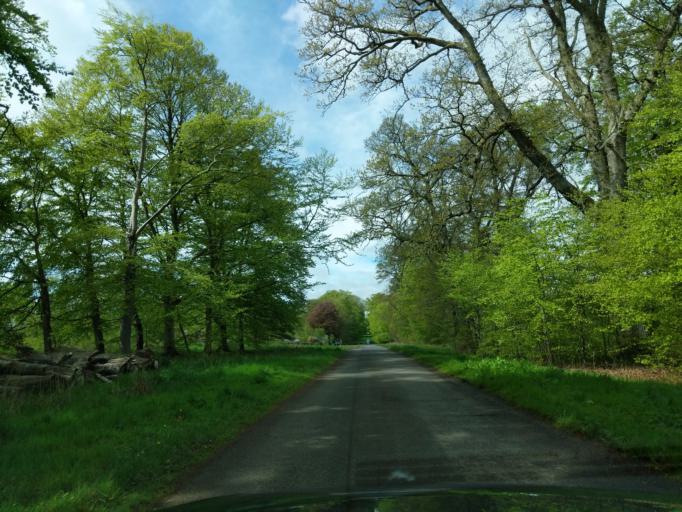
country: GB
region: Scotland
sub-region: The Scottish Borders
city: Saint Boswells
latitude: 55.6487
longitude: -2.5578
